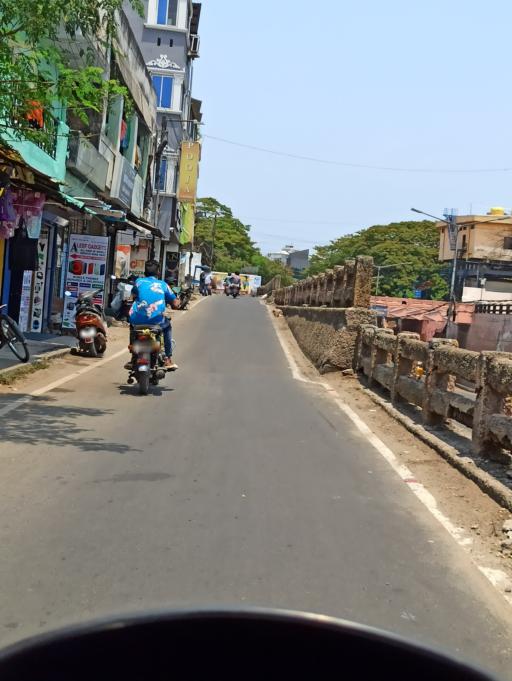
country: IN
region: Tamil Nadu
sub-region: Chennai
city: Chetput
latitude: 13.0664
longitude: 80.2319
